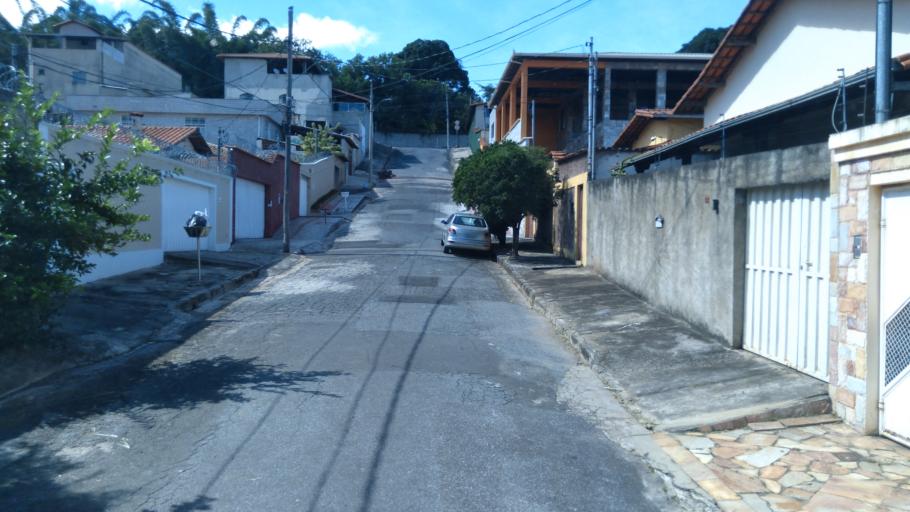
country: BR
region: Minas Gerais
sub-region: Belo Horizonte
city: Belo Horizonte
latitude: -19.8483
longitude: -43.9139
